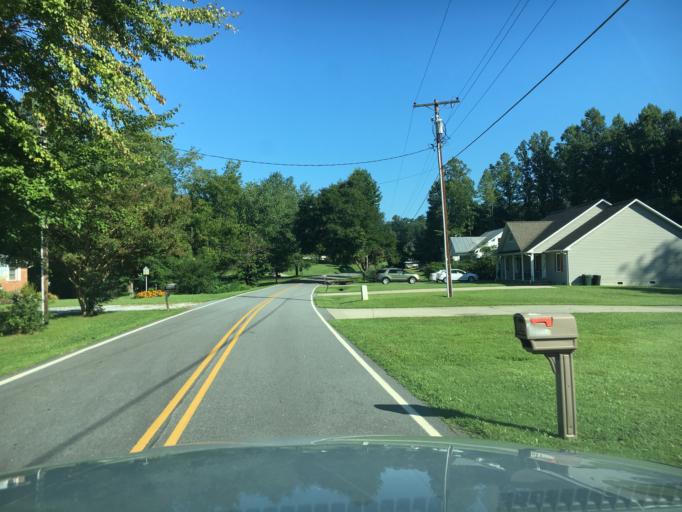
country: US
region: North Carolina
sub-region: McDowell County
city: West Marion
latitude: 35.6466
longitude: -82.0205
